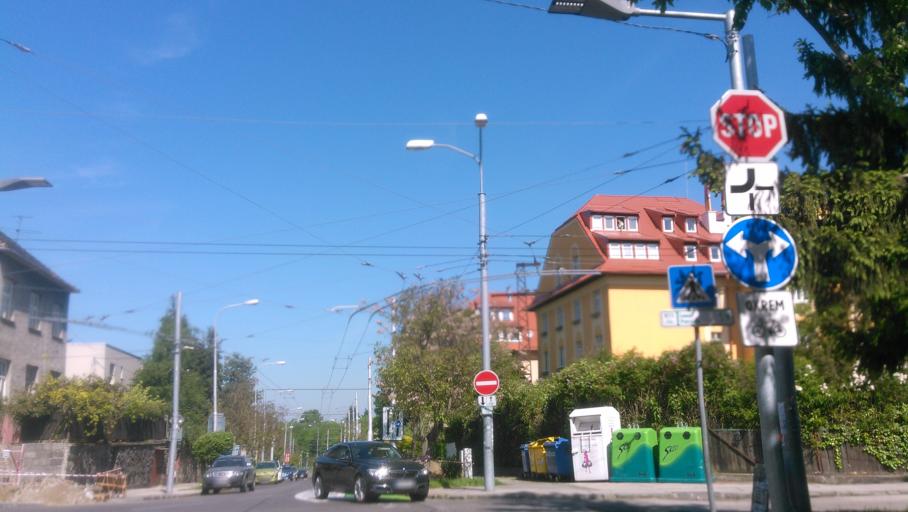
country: SK
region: Bratislavsky
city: Bratislava
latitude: 48.1624
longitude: 17.0899
